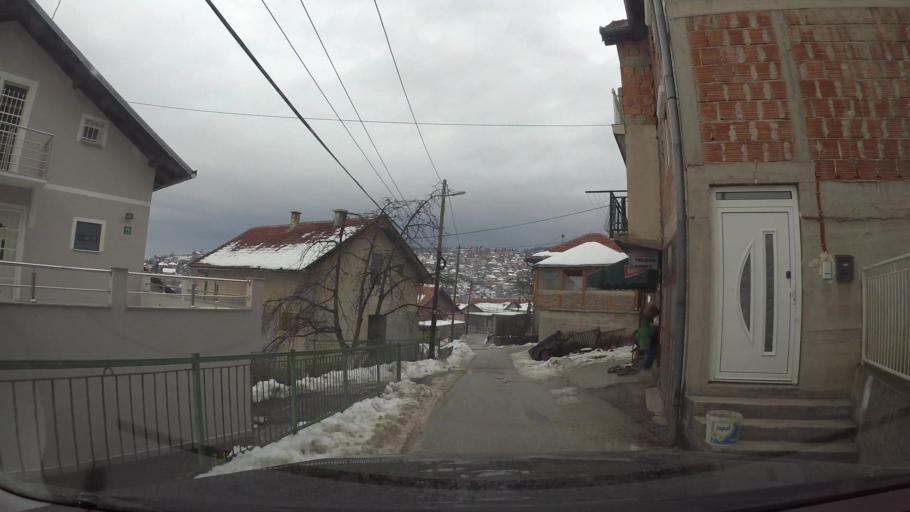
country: BA
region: Federation of Bosnia and Herzegovina
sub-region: Kanton Sarajevo
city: Sarajevo
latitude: 43.8552
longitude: 18.3482
